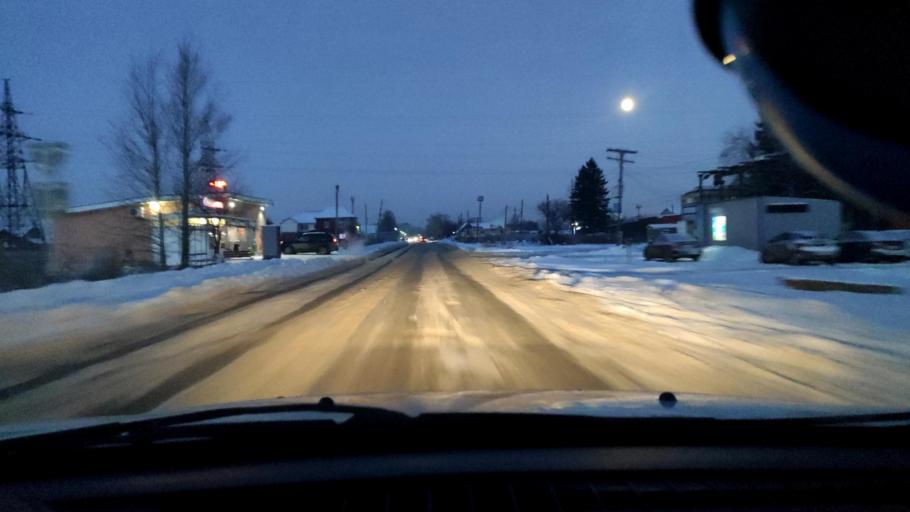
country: RU
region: Perm
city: Kultayevo
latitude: 57.8880
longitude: 55.9244
